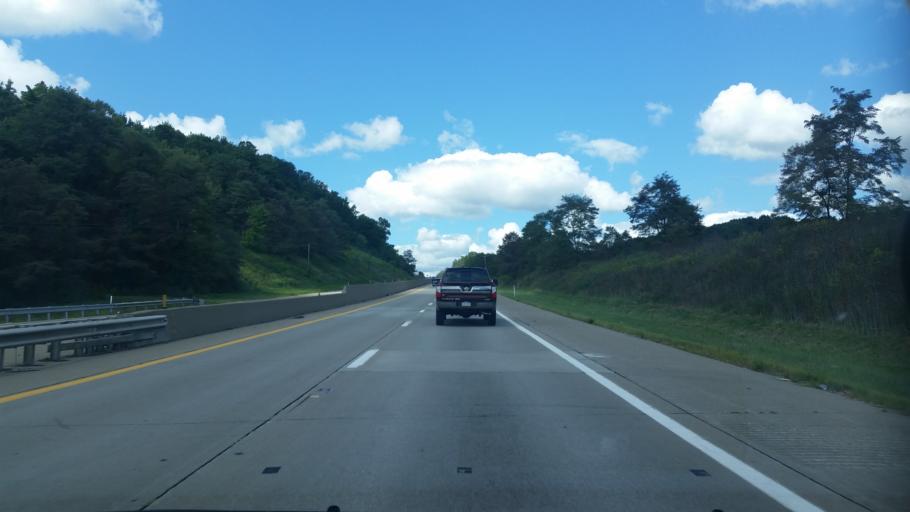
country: US
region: Pennsylvania
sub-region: Westmoreland County
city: Delmont
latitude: 40.3993
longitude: -79.5061
